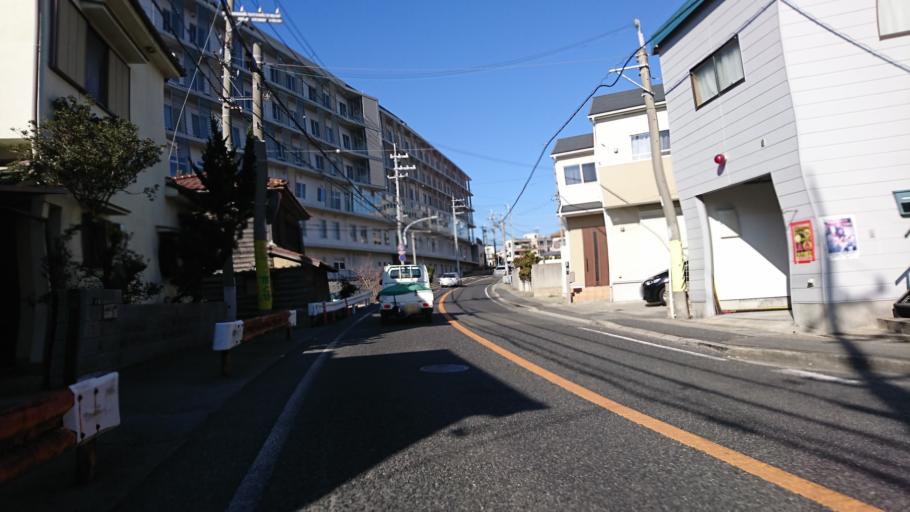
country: JP
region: Hyogo
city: Akashi
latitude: 34.6602
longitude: 134.9506
